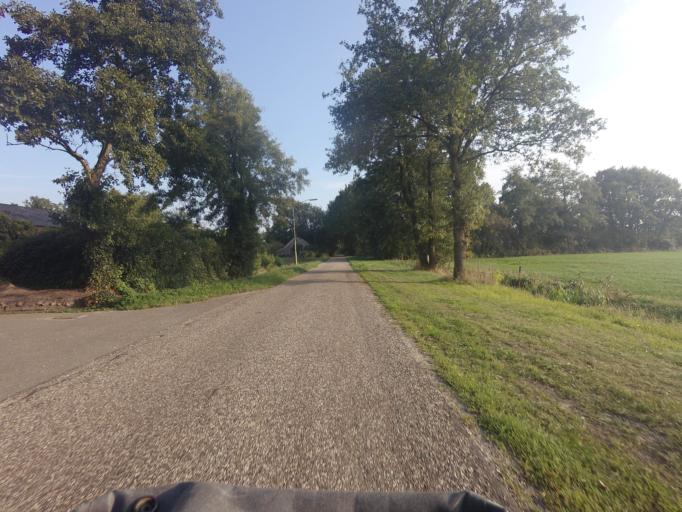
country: NL
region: Drenthe
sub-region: Gemeente Tynaarlo
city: Vries
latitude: 53.1101
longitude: 6.5241
